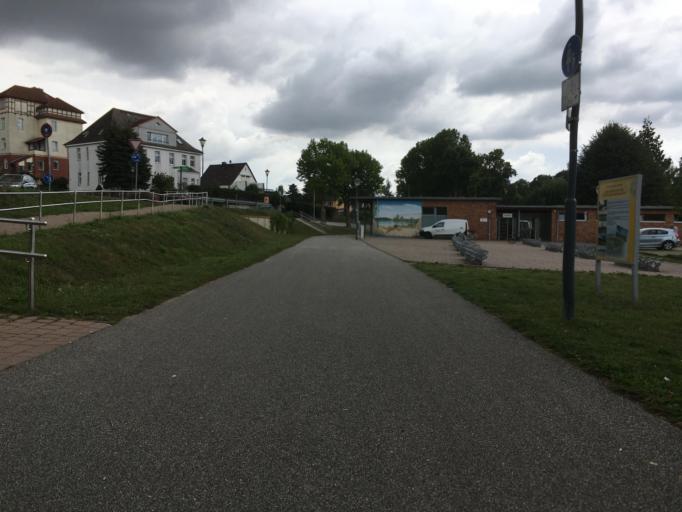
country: DE
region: Brandenburg
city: Prenzlau
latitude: 53.3070
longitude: 13.8605
